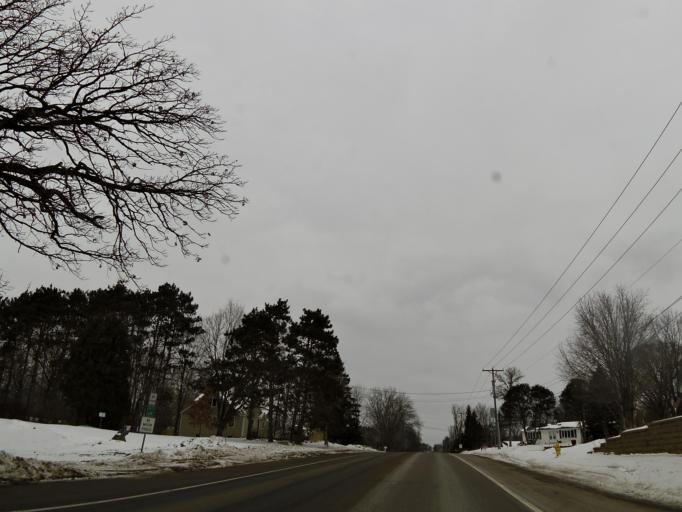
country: US
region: Minnesota
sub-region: Washington County
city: Oak Park Heights
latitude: 45.0288
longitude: -92.8073
